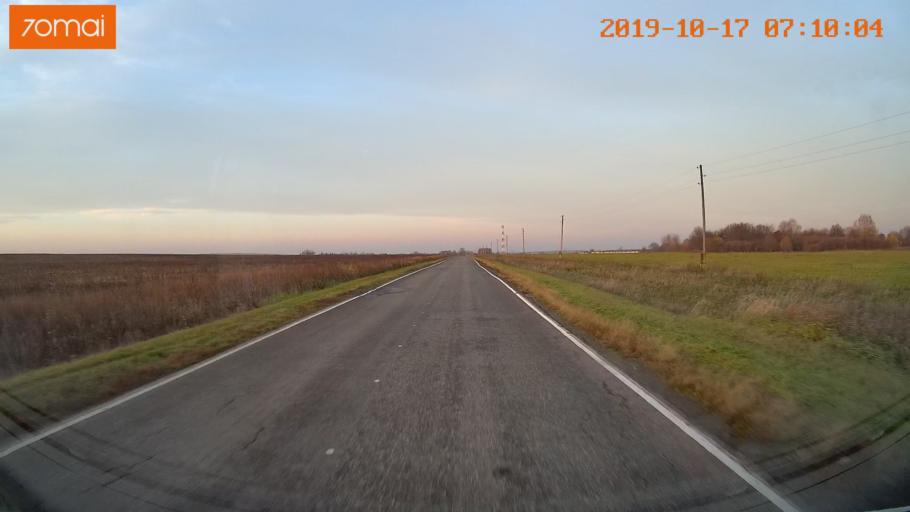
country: RU
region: Vladimir
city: Suzdal'
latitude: 56.4143
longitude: 40.3694
